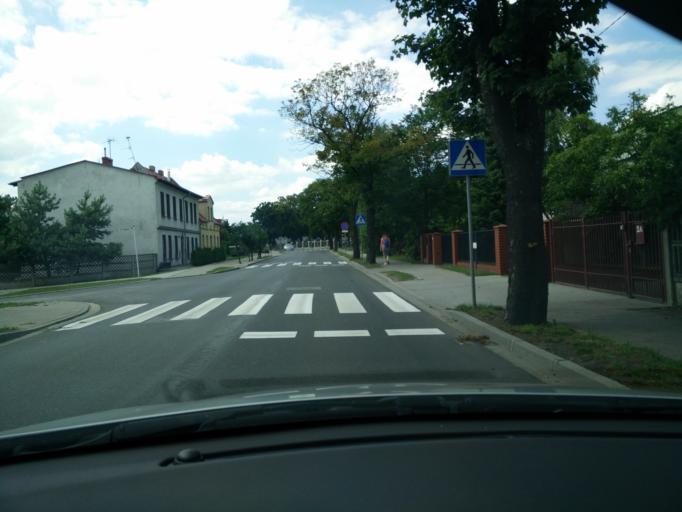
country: PL
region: Greater Poland Voivodeship
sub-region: Powiat sredzki
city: Sroda Wielkopolska
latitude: 52.2312
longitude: 17.2852
